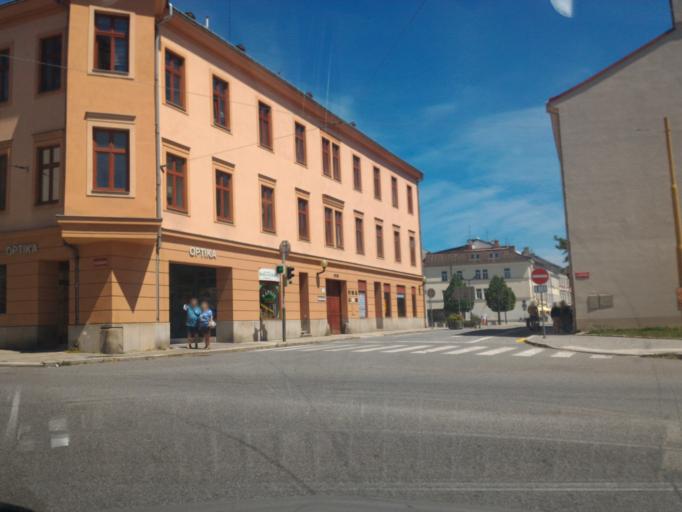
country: CZ
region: Vysocina
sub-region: Okres Jihlava
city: Jihlava
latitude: 49.3952
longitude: 15.5856
